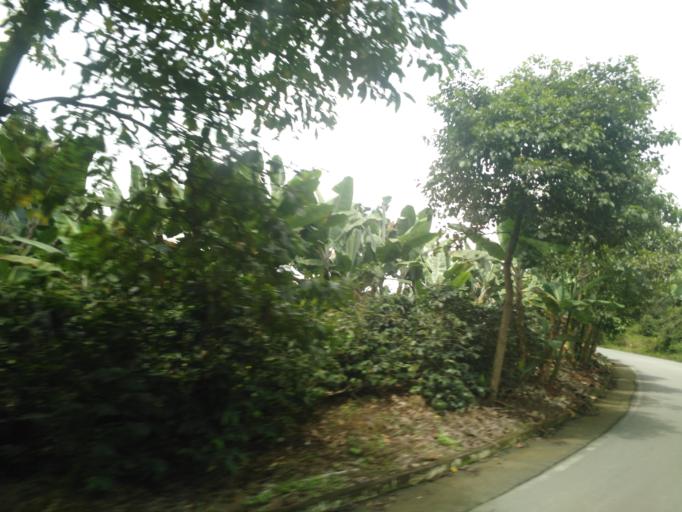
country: CO
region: Valle del Cauca
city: Sevilla
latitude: 4.2977
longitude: -75.9021
